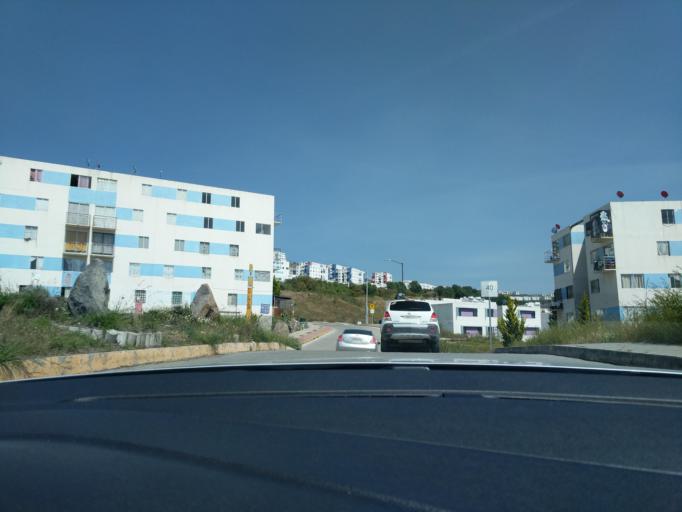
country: MX
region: Hidalgo
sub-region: Atotonilco de Tula
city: Paseos de la Pradera
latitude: 19.8961
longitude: -99.2389
